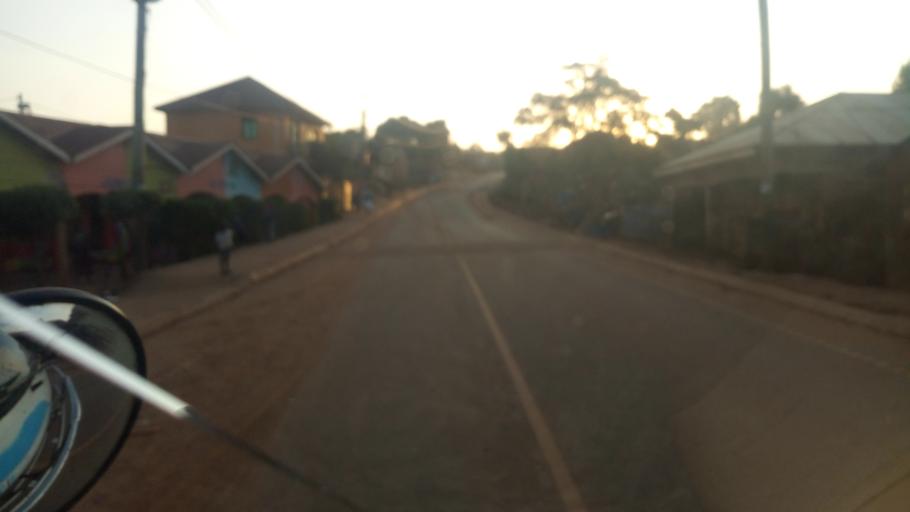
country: UG
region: Central Region
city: Kampala Central Division
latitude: 0.3618
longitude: 32.5591
